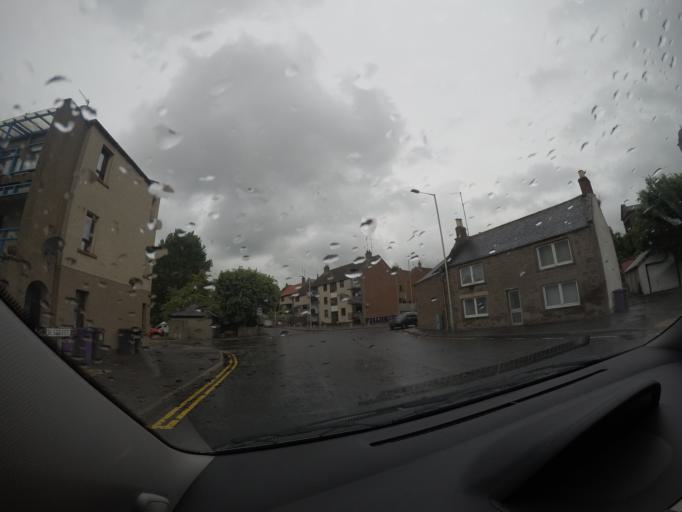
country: GB
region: Scotland
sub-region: Angus
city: Brechin
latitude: 56.7270
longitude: -2.6537
